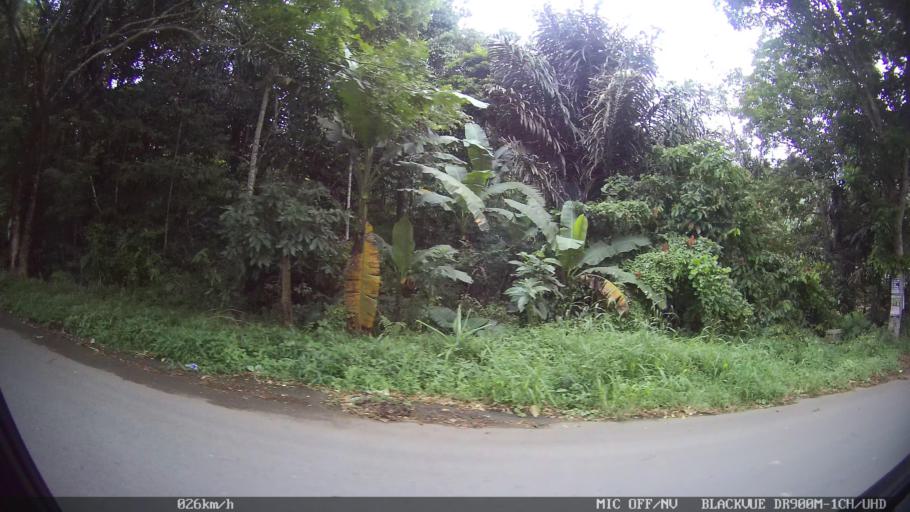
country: ID
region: Lampung
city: Bandarlampung
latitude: -5.4205
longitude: 105.1857
